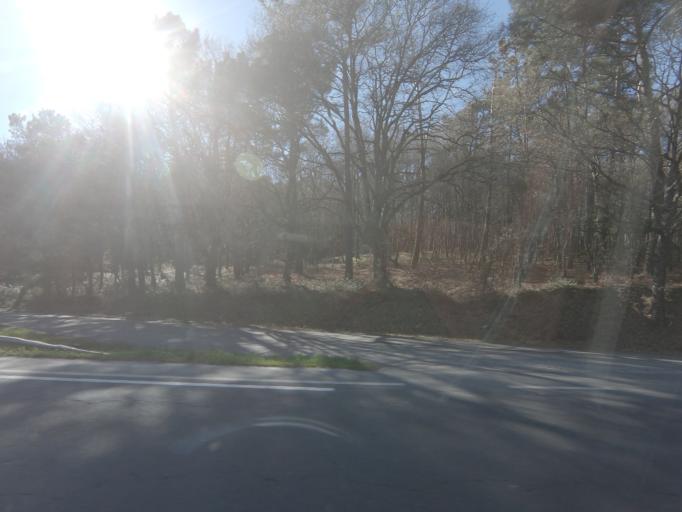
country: ES
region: Galicia
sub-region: Provincia de Pontevedra
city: Silleda
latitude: 42.6888
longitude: -8.2206
